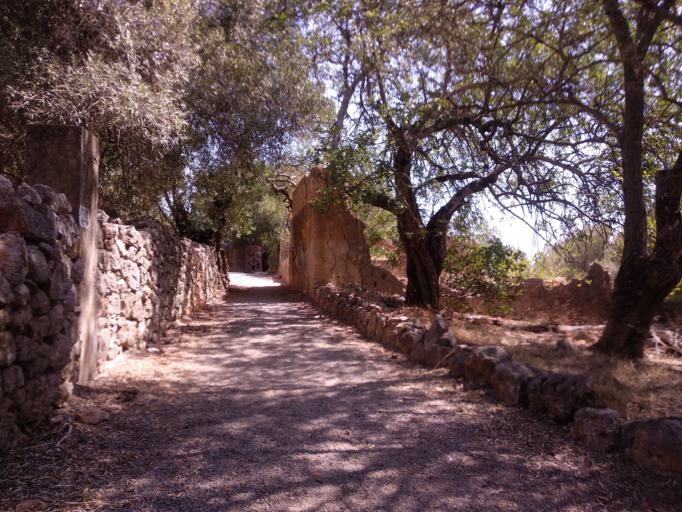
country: PT
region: Faro
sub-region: Sao Bras de Alportel
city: Sao Bras de Alportel
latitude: 37.1493
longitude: -7.8882
